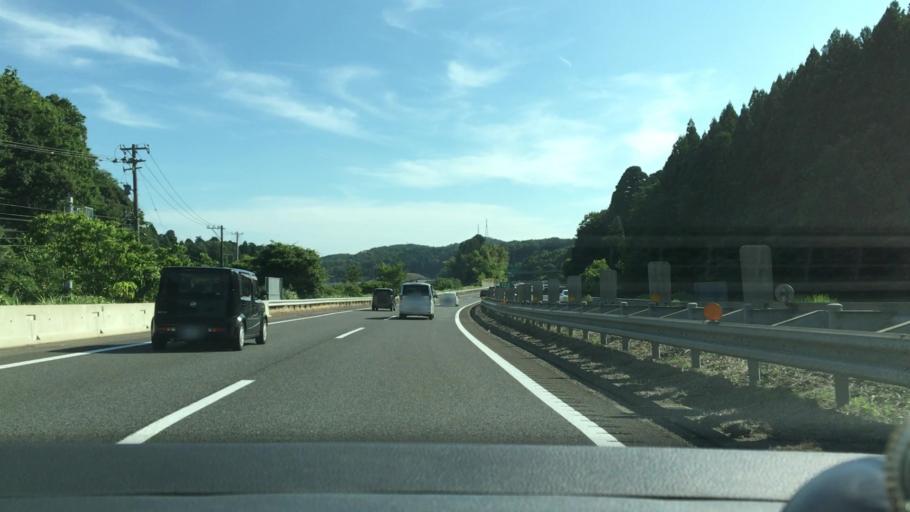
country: JP
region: Fukui
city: Maruoka
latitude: 36.2441
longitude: 136.2850
